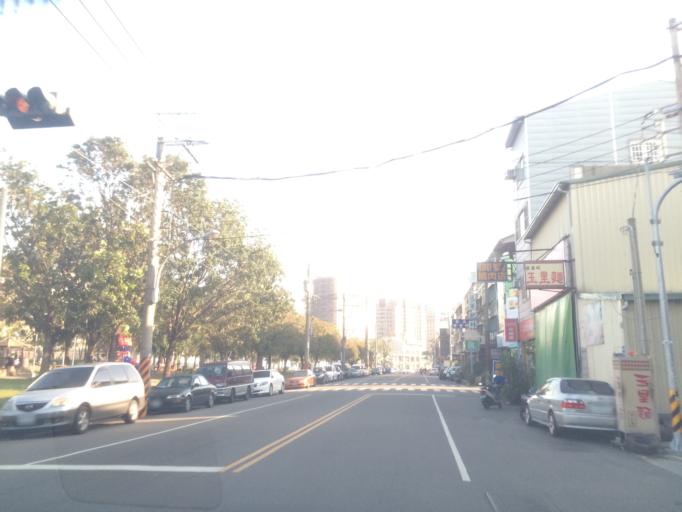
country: TW
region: Taiwan
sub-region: Taichung City
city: Taichung
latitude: 24.1904
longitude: 120.6851
